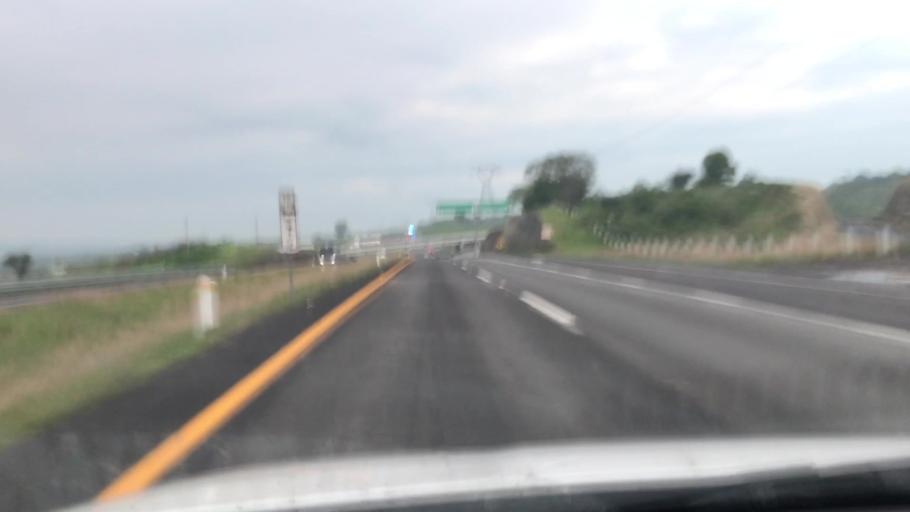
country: MX
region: Jalisco
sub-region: Zapotlanejo
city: La Mezquitera
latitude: 20.5839
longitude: -103.0966
